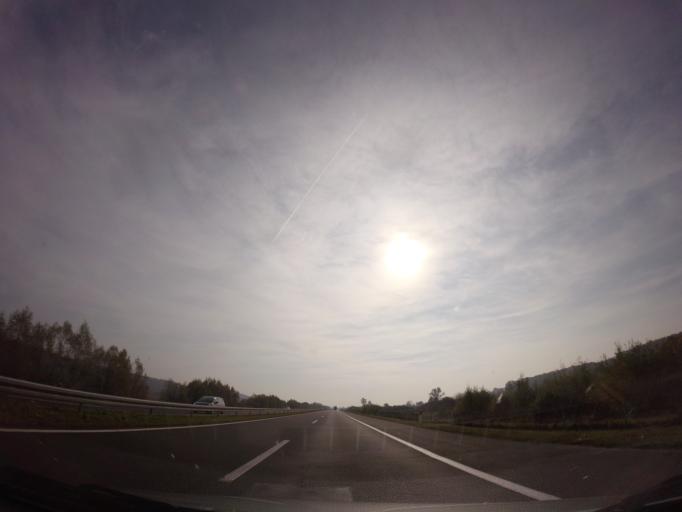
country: HR
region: Varazdinska
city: Remetinec
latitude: 46.0259
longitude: 16.2948
